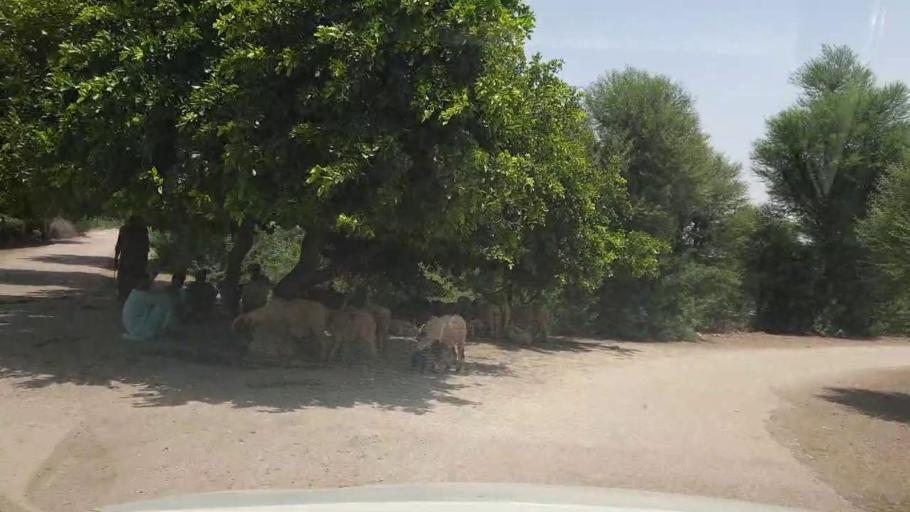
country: PK
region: Sindh
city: Bozdar
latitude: 27.2054
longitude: 68.6681
